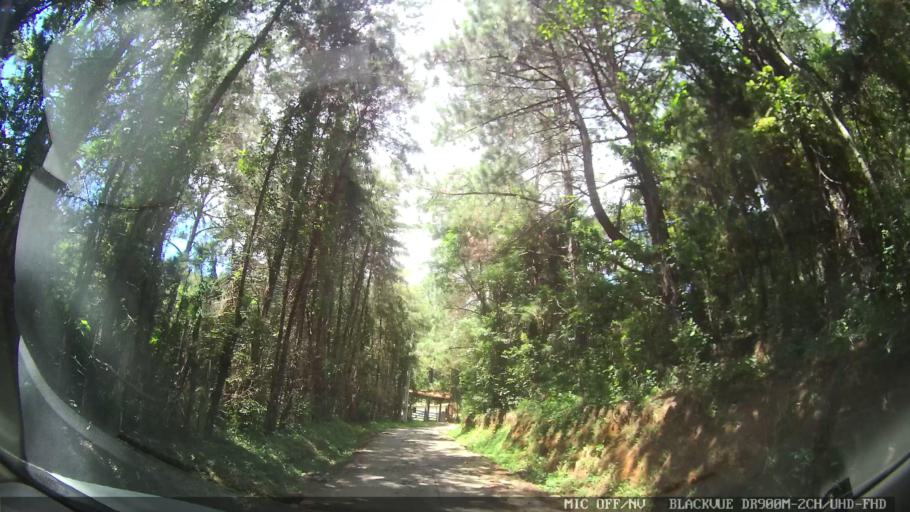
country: BR
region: Minas Gerais
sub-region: Extrema
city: Extrema
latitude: -22.8752
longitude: -46.3235
